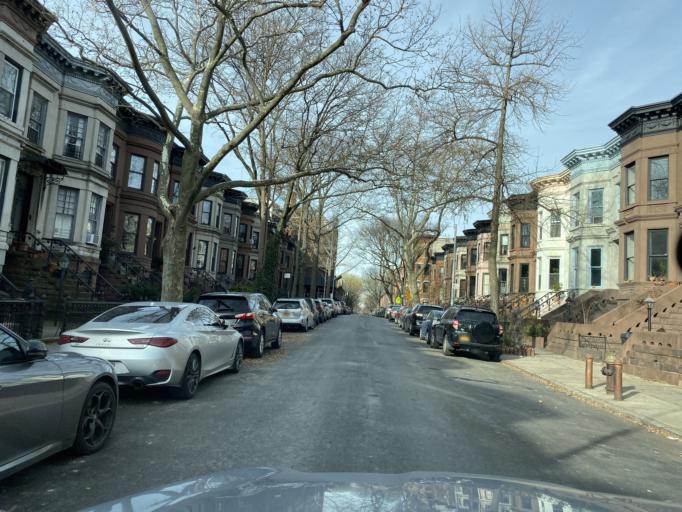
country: US
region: New York
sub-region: Kings County
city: Brooklyn
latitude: 40.6627
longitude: -73.9798
